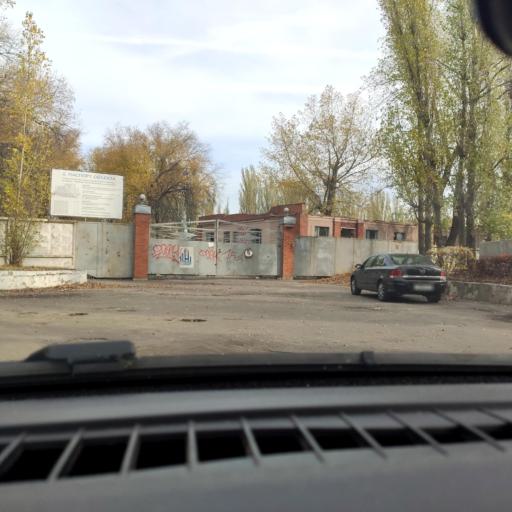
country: RU
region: Voronezj
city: Voronezh
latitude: 51.6460
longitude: 39.1513
